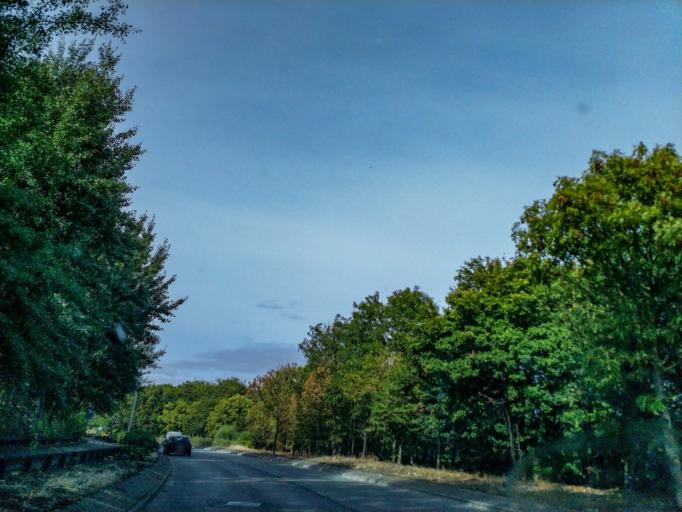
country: GB
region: England
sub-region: City and Borough of Birmingham
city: Birmingham
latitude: 52.5015
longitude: -1.8561
